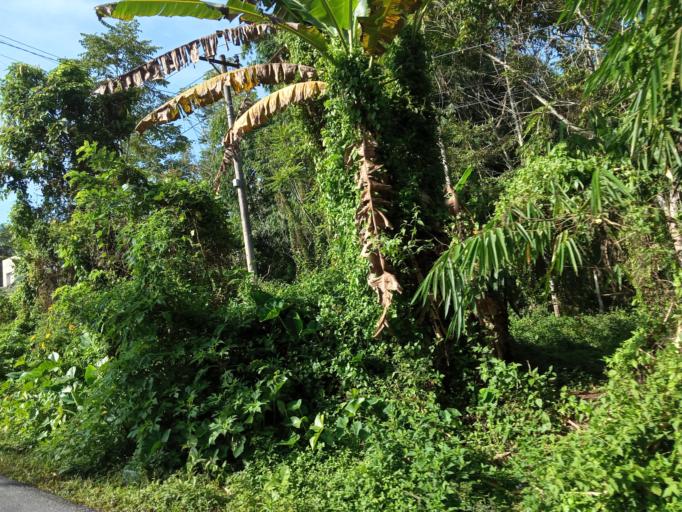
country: ID
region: Jambi
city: Sungai Penuh
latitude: -2.0988
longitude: 101.4626
